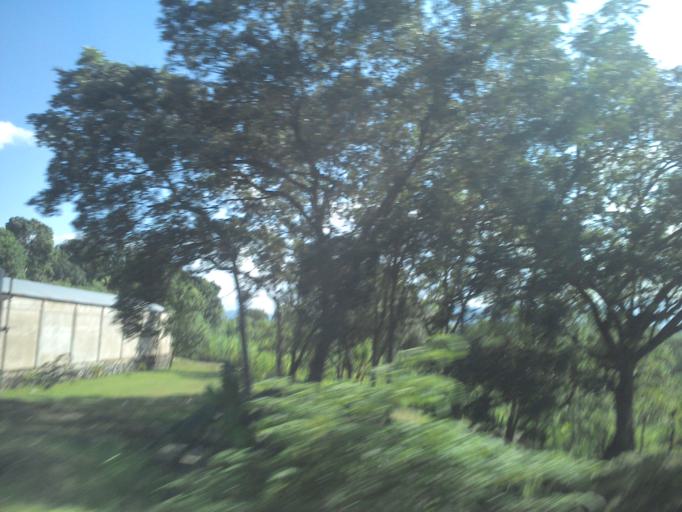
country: MX
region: Chiapas
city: Palenque
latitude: 17.5525
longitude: -91.9880
